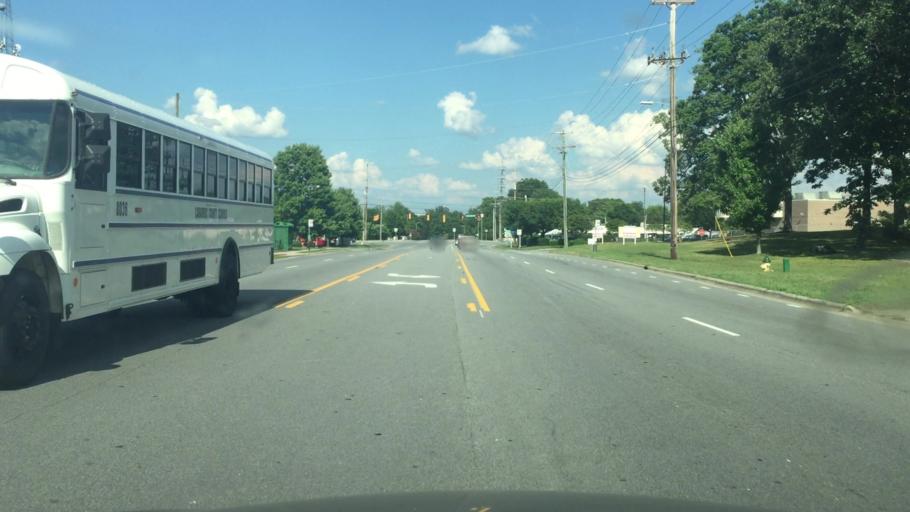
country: US
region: North Carolina
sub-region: Cabarrus County
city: Concord
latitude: 35.3961
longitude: -80.6092
